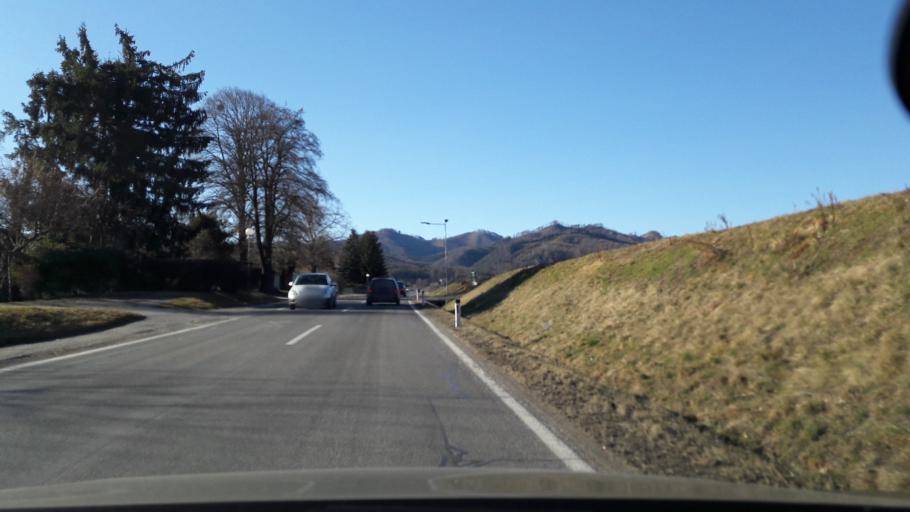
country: AT
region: Styria
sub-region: Politischer Bezirk Graz-Umgebung
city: Gratwein
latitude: 47.1330
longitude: 15.3051
